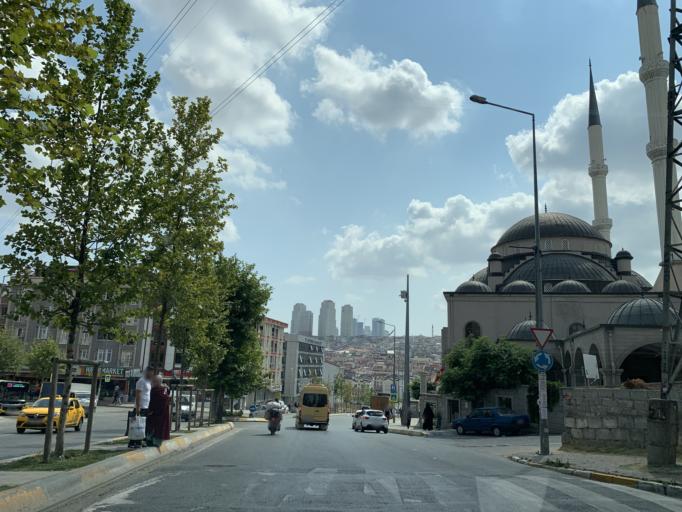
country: TR
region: Istanbul
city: Esenyurt
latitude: 41.0418
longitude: 28.6608
